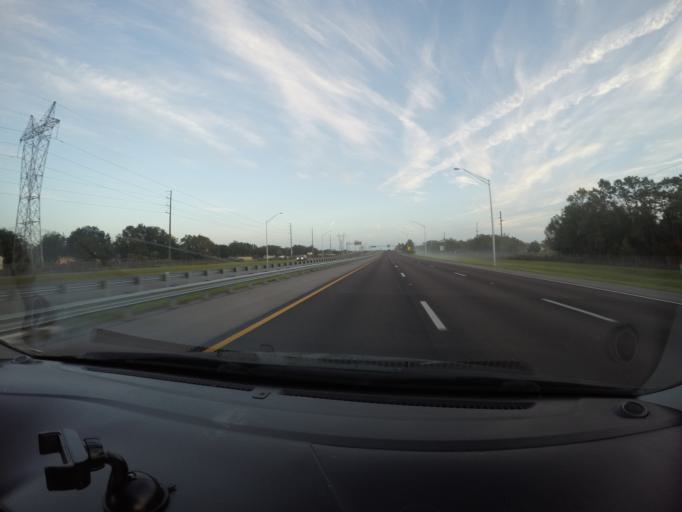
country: US
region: Florida
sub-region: Orange County
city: Azalea Park
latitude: 28.5203
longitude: -81.2508
